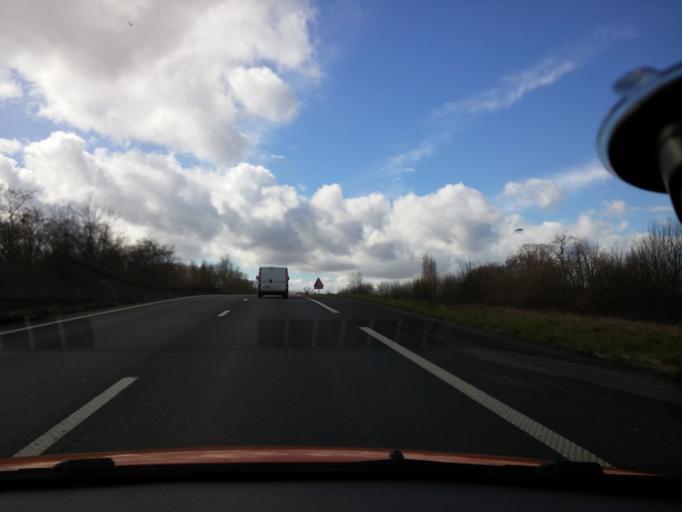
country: FR
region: Ile-de-France
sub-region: Departement de l'Essonne
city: Champlan
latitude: 48.7144
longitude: 2.2888
